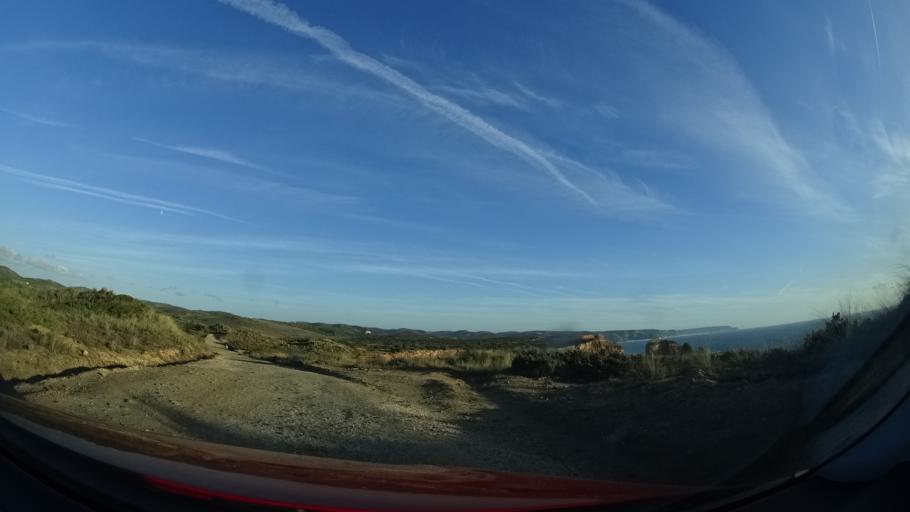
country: PT
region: Faro
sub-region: Vila do Bispo
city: Vila do Bispo
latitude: 37.1823
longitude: -8.9097
